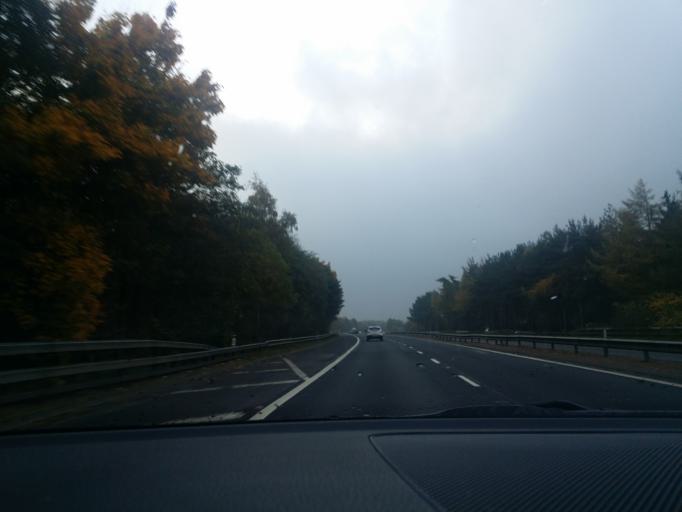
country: GB
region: Scotland
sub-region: Stirling
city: Cowie
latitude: 56.0553
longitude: -3.8469
